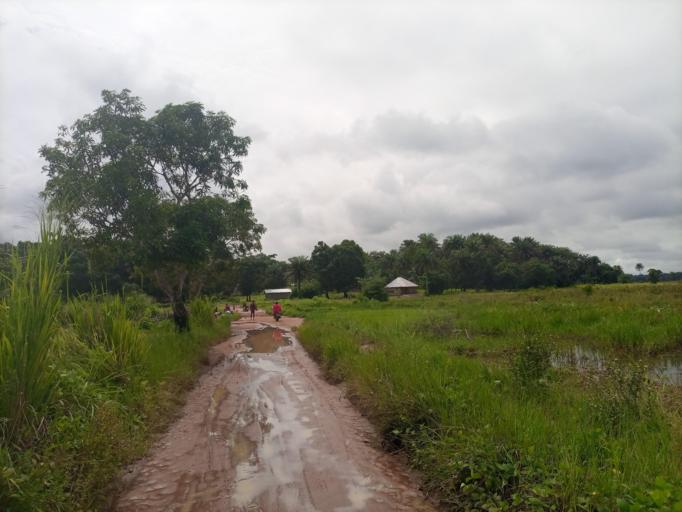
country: SL
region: Northern Province
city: Sawkta
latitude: 8.6349
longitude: -13.1999
